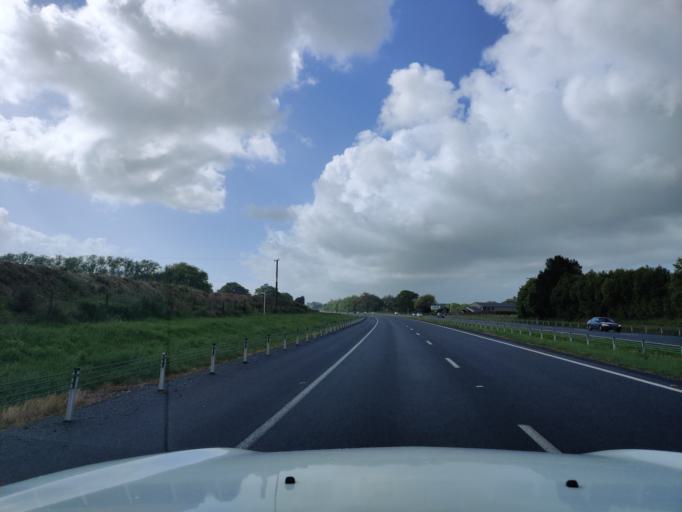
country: NZ
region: Waikato
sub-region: Waipa District
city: Cambridge
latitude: -37.8382
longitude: 175.3677
